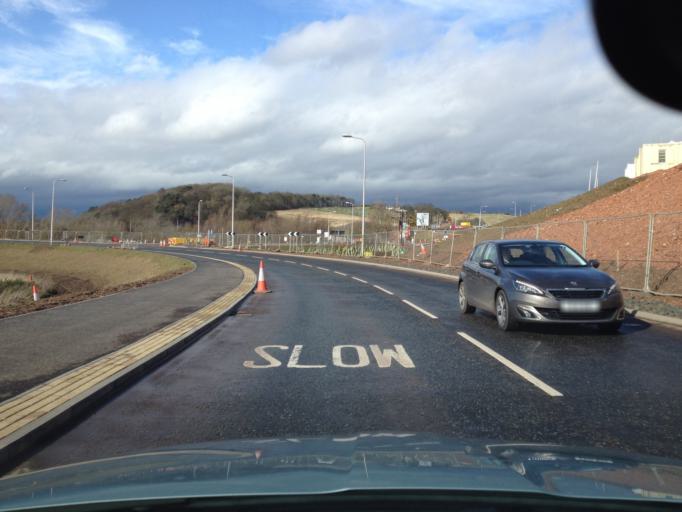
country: GB
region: Scotland
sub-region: Fife
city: North Queensferry
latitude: 56.0177
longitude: -3.4064
